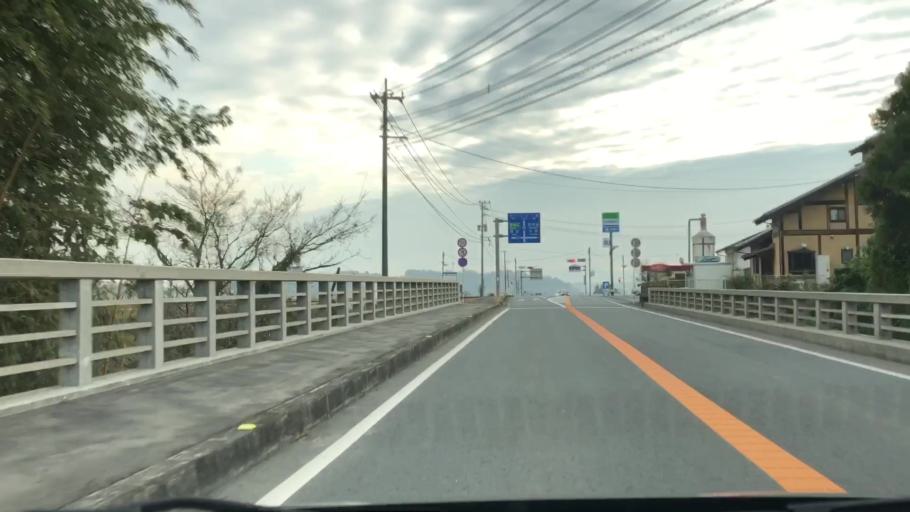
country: JP
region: Oita
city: Takedamachi
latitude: 32.9697
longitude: 131.4636
